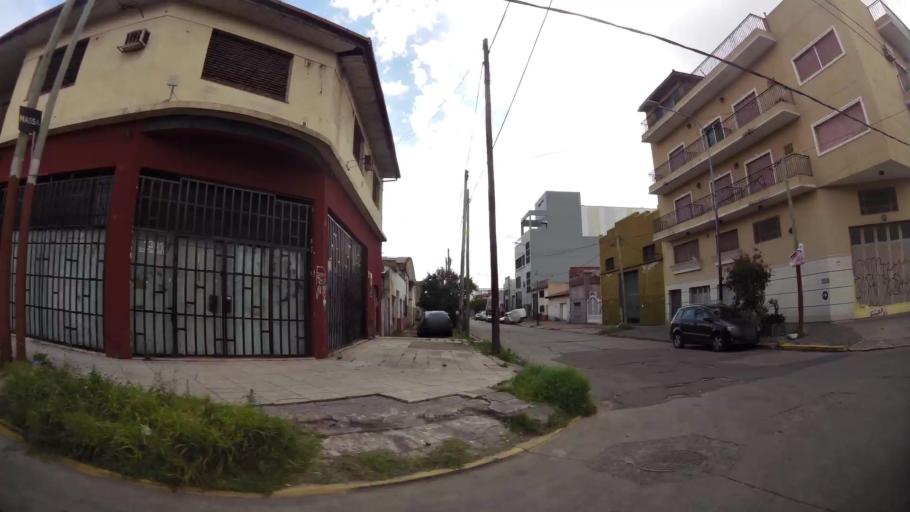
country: AR
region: Buenos Aires
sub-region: Partido de Lanus
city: Lanus
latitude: -34.6960
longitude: -58.3720
